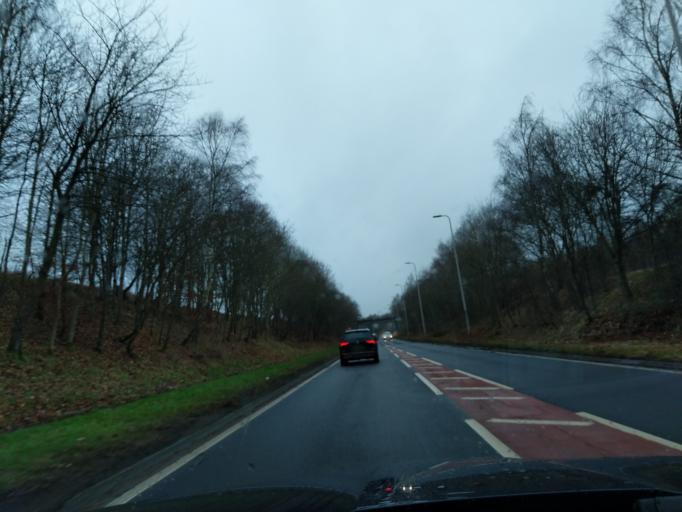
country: GB
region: Scotland
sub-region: The Scottish Borders
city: Melrose
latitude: 55.5995
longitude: -2.7471
